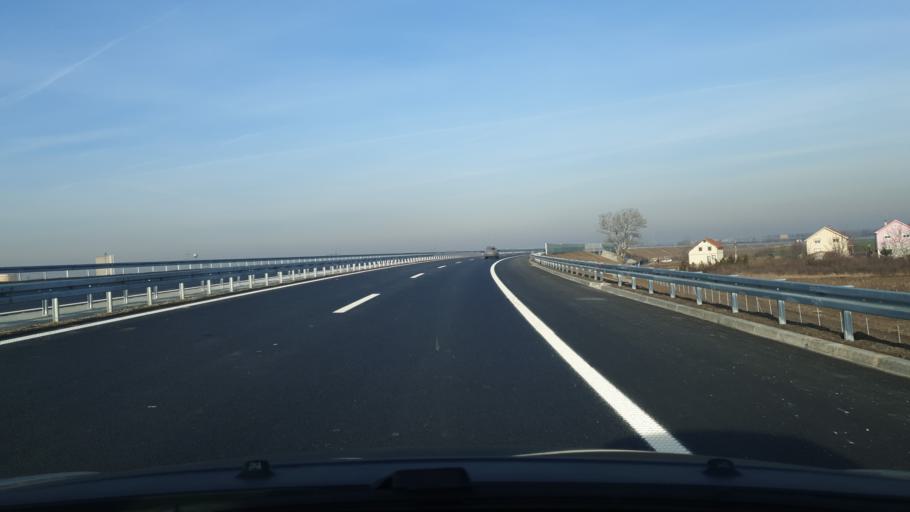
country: RS
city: Becmen
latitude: 44.7632
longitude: 20.2457
